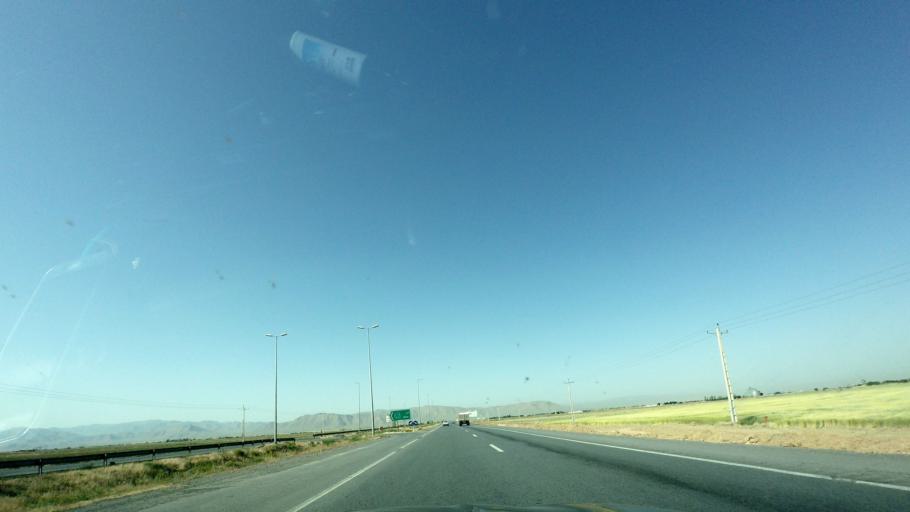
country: IR
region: Markazi
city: Ashtian
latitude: 34.1980
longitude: 50.0594
